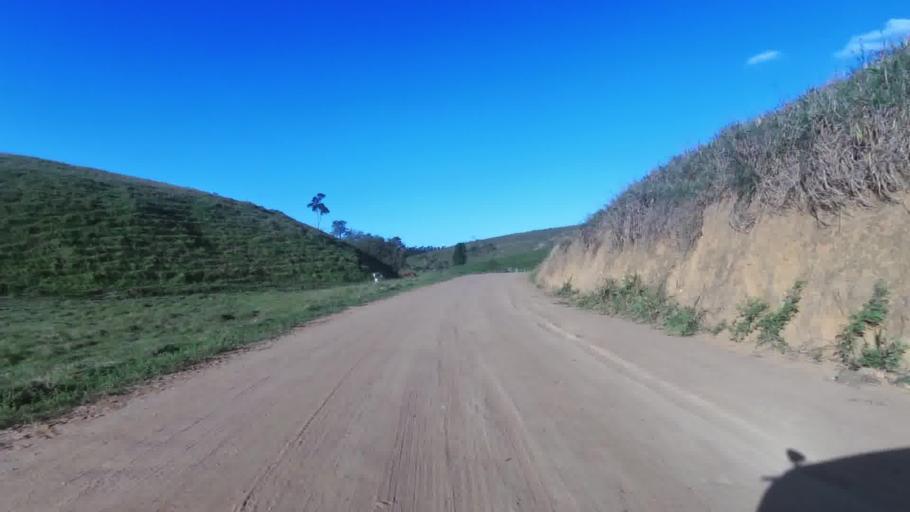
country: BR
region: Espirito Santo
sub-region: Marataizes
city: Marataizes
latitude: -21.1432
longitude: -41.0266
